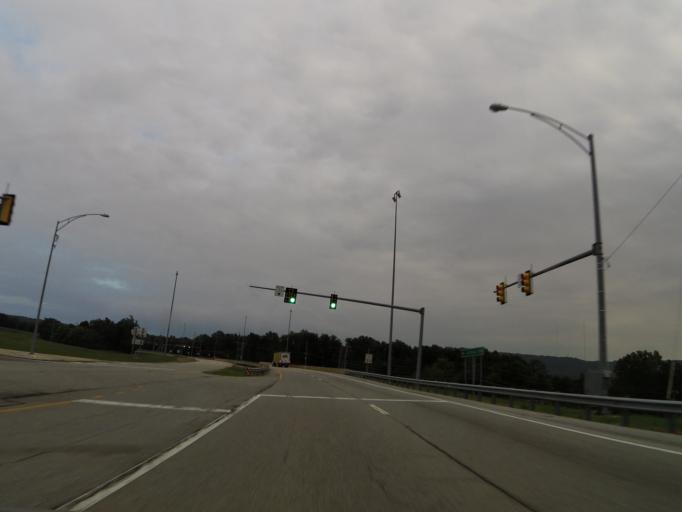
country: US
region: Alabama
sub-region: Madison County
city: Huntsville
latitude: 34.7585
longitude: -86.5664
